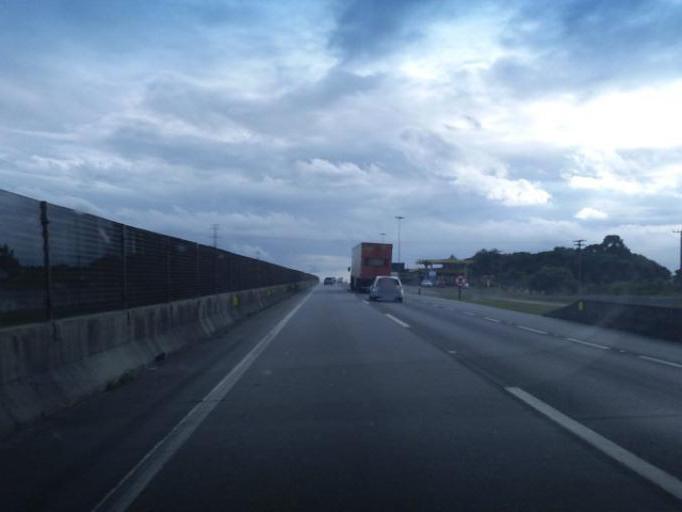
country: BR
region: Parana
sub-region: Piraquara
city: Piraquara
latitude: -25.4913
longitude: -49.1132
